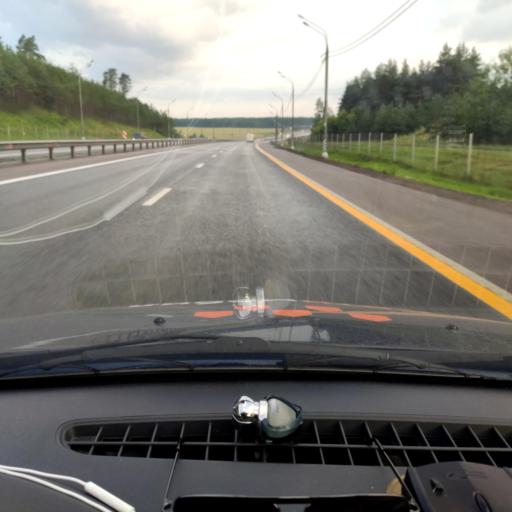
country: RU
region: Lipetsk
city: Zadonsk
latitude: 52.3391
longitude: 38.9674
